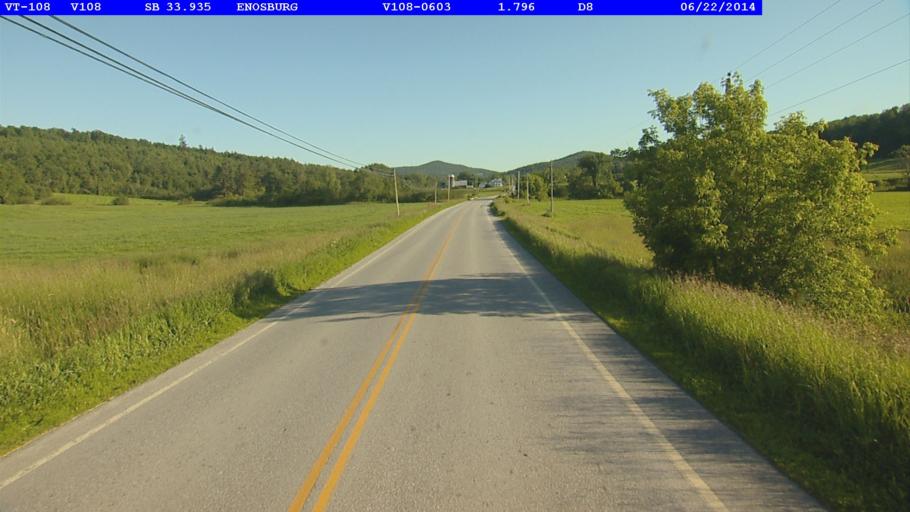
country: US
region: Vermont
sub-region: Franklin County
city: Enosburg Falls
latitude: 44.8633
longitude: -72.7994
